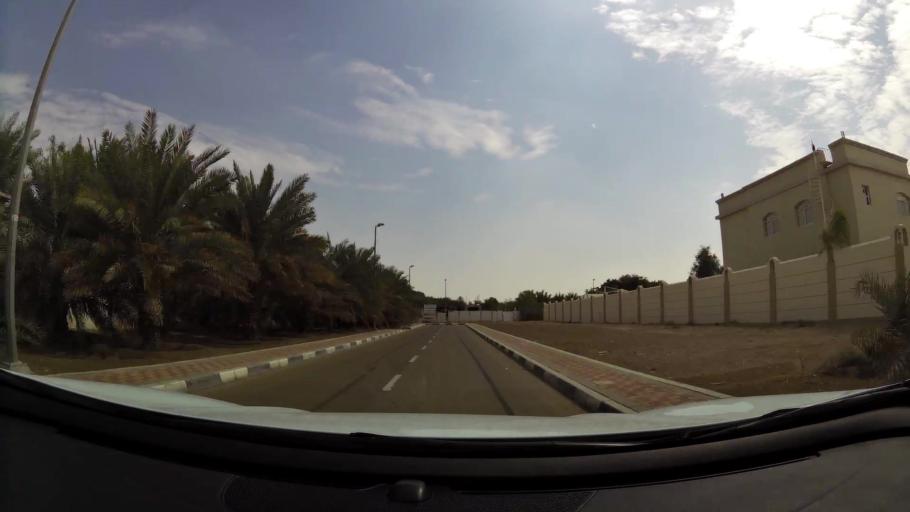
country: AE
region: Abu Dhabi
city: Al Ain
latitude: 24.1920
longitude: 55.7981
